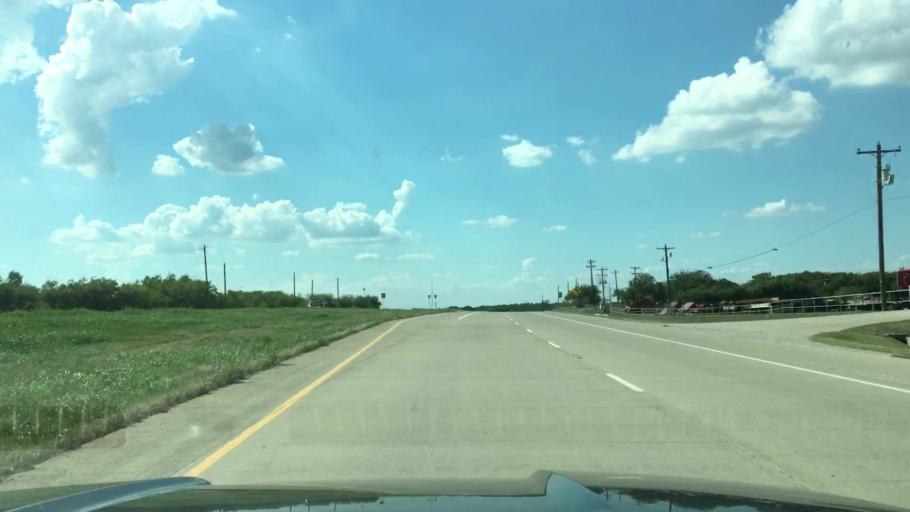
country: US
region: Texas
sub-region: Wise County
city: Rhome
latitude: 33.0426
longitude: -97.4499
